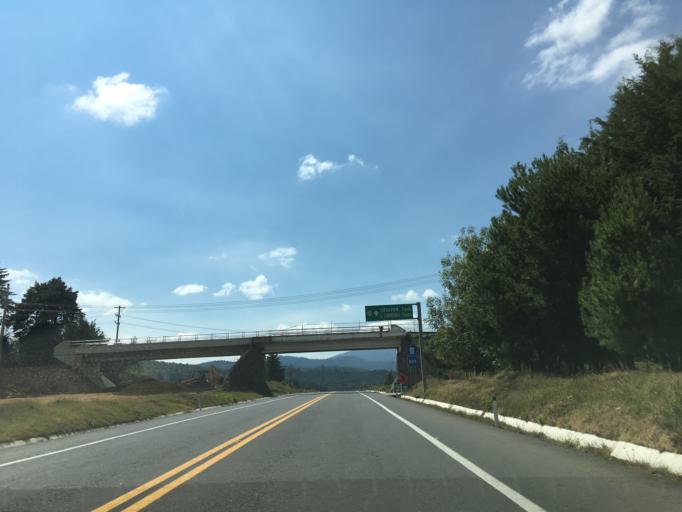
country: MX
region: Michoacan
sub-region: Patzcuaro
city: Colonia Vista Bella (Lomas del Peaje)
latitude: 19.4976
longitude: -101.5908
